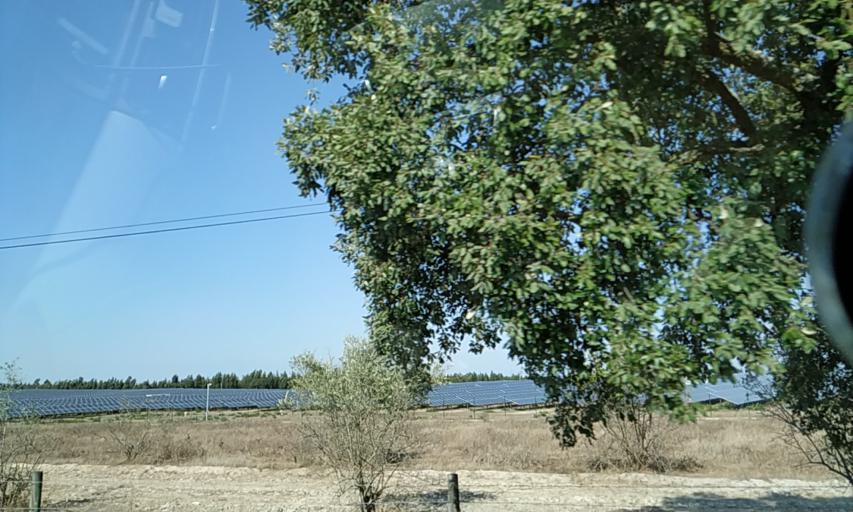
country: PT
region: Evora
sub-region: Vendas Novas
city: Vendas Novas
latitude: 38.7235
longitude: -8.6204
